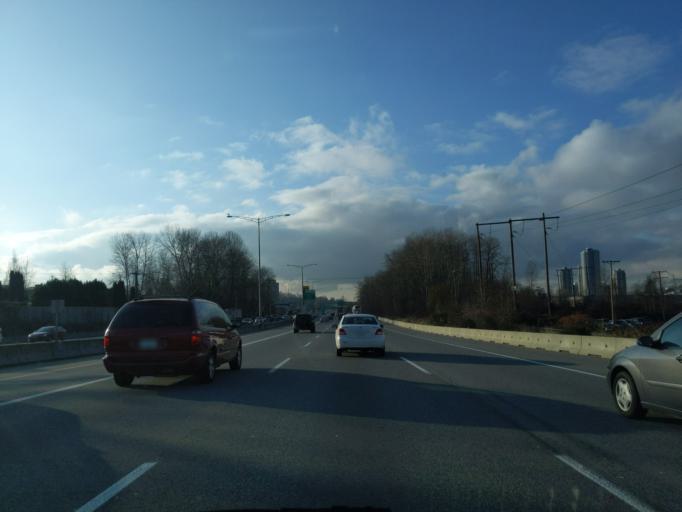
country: CA
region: British Columbia
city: Burnaby
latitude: 49.2591
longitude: -122.9905
